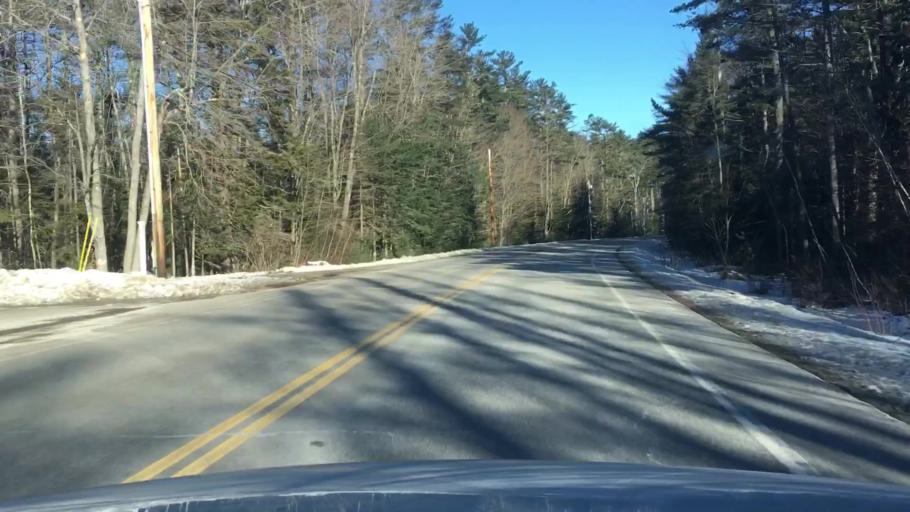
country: US
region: Maine
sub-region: Androscoggin County
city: Lisbon Falls
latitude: 43.9590
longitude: -70.1236
